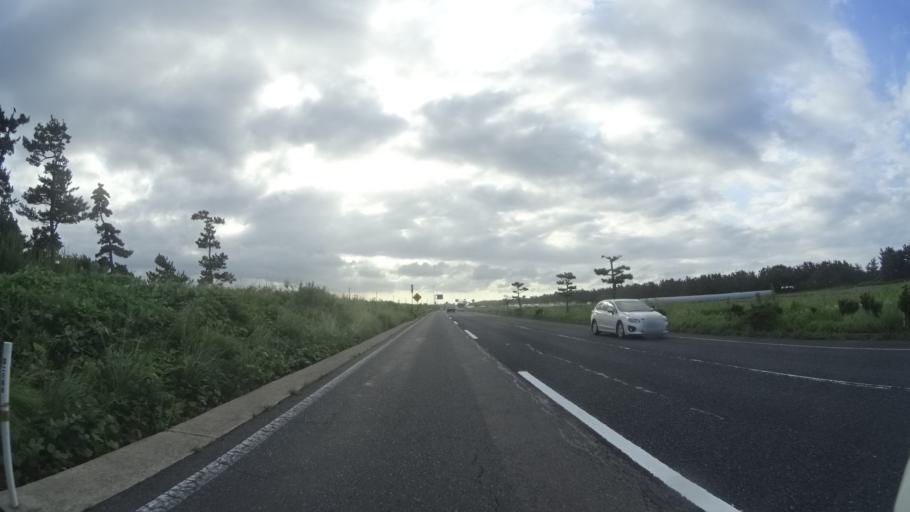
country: JP
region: Tottori
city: Kurayoshi
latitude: 35.4983
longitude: 133.7797
